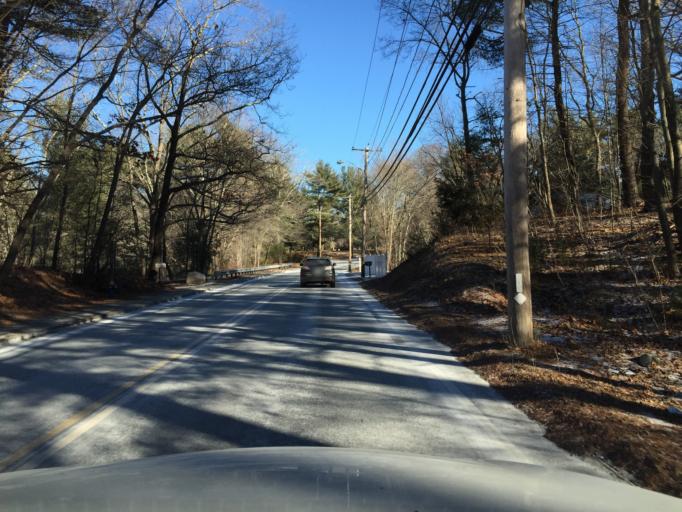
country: US
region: Massachusetts
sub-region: Bristol County
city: Mansfield
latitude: 42.0632
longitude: -71.2128
